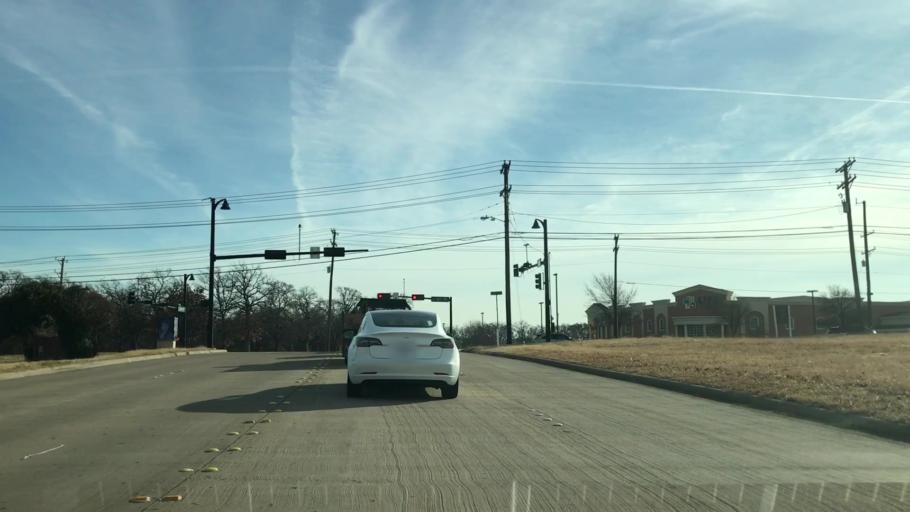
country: US
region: Texas
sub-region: Tarrant County
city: Colleyville
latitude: 32.8913
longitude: -97.2041
